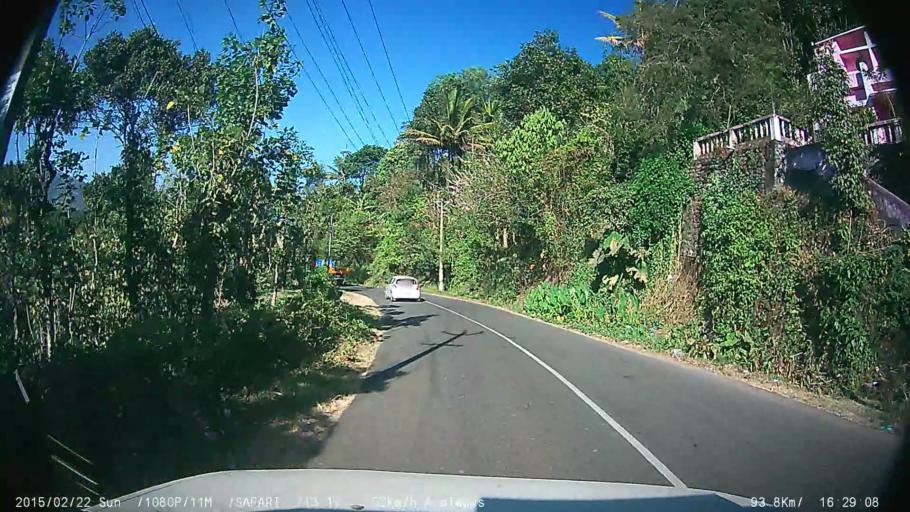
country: IN
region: Tamil Nadu
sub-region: Theni
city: Gudalur
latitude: 9.6128
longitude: 77.1519
